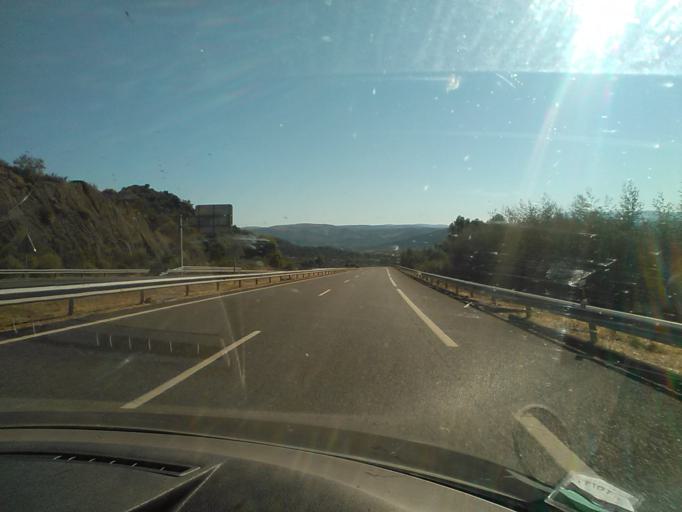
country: ES
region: Galicia
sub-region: Provincia de Ourense
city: Verin
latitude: 41.9326
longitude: -7.4025
